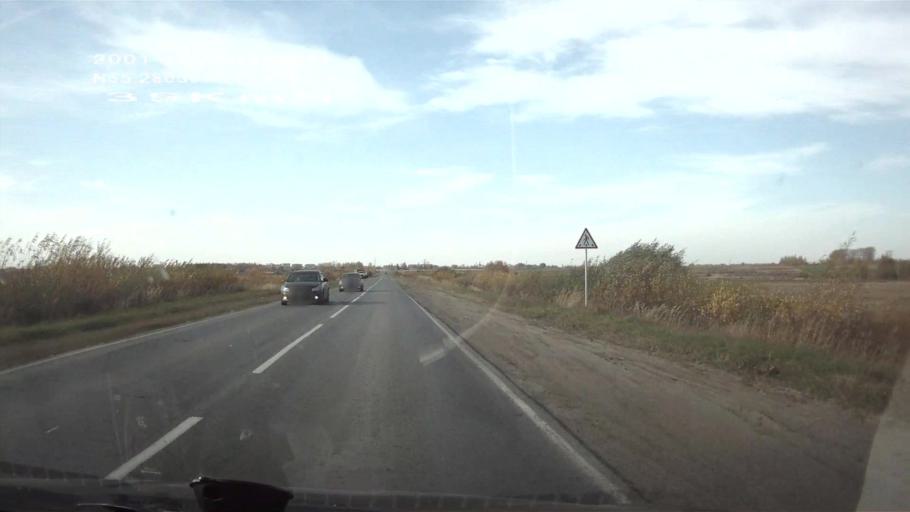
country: RU
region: Chuvashia
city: Ibresi
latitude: 55.2864
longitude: 47.0795
